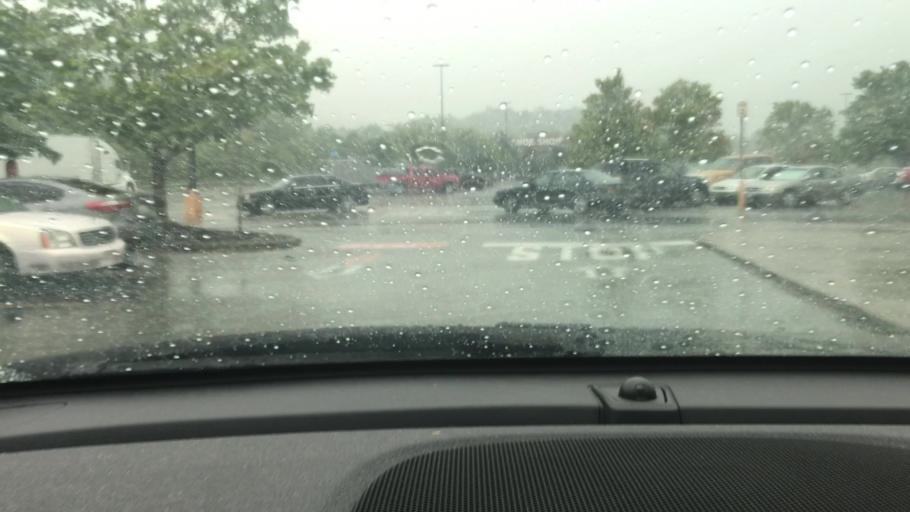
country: US
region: Tennessee
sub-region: Cheatham County
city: Ashland City
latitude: 36.2476
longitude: -87.0335
